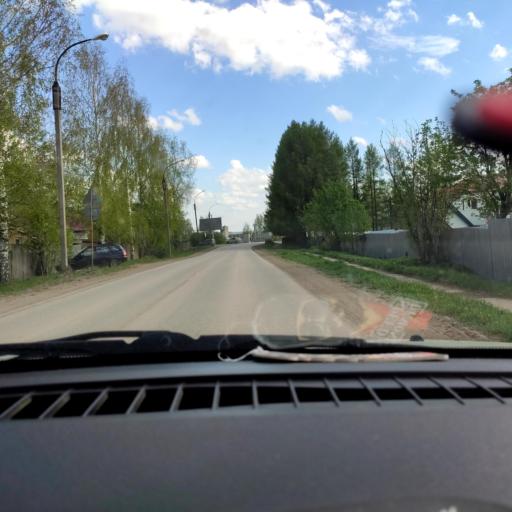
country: RU
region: Perm
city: Kudymkar
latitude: 59.0162
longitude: 54.6520
